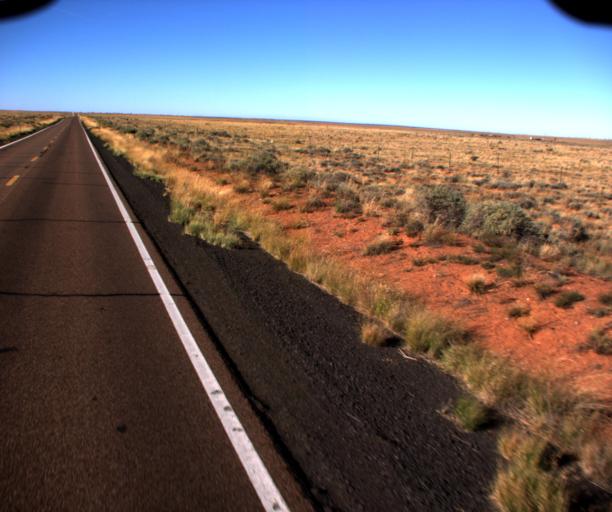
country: US
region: Arizona
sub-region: Navajo County
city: Holbrook
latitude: 34.7888
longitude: -110.2225
